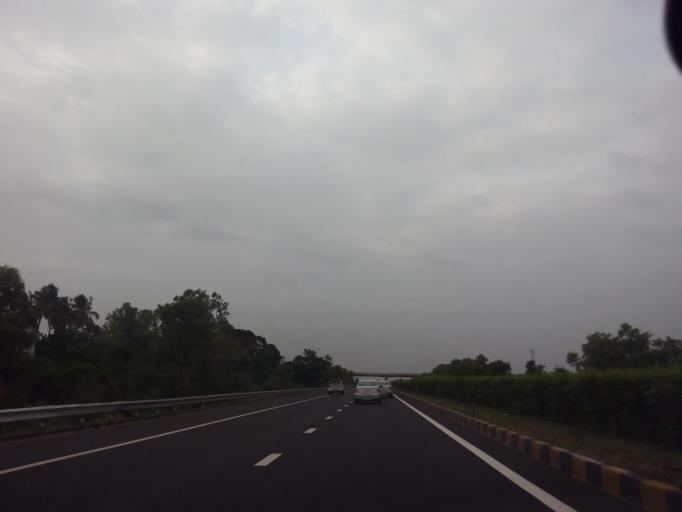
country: IN
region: Gujarat
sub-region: Kheda
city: Chaklasi
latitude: 22.6507
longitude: 72.9290
